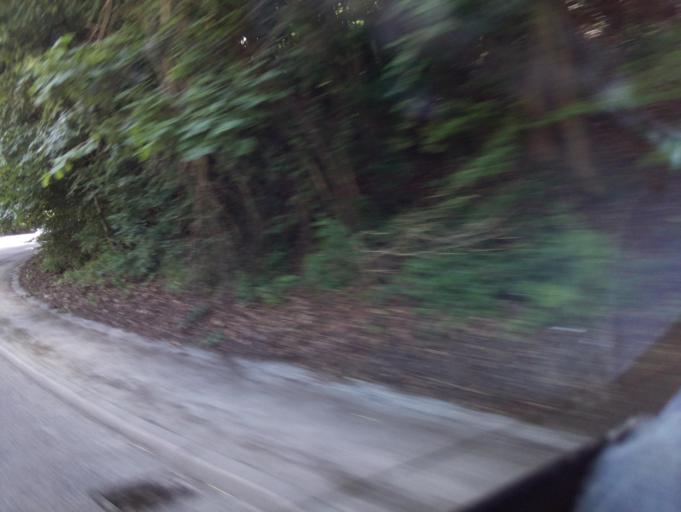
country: GB
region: England
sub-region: Derbyshire
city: Buxton
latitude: 53.2478
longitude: -1.9057
